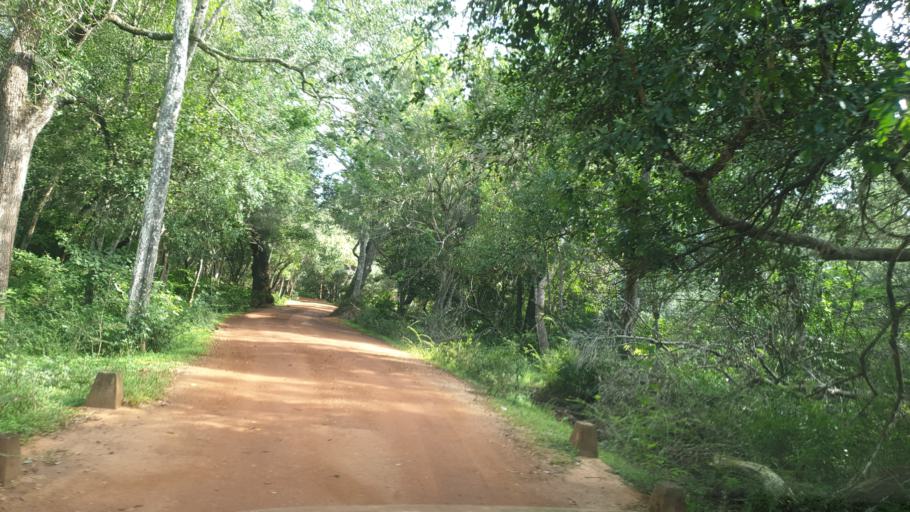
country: LK
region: North Central
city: Anuradhapura
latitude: 8.3780
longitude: 80.0697
